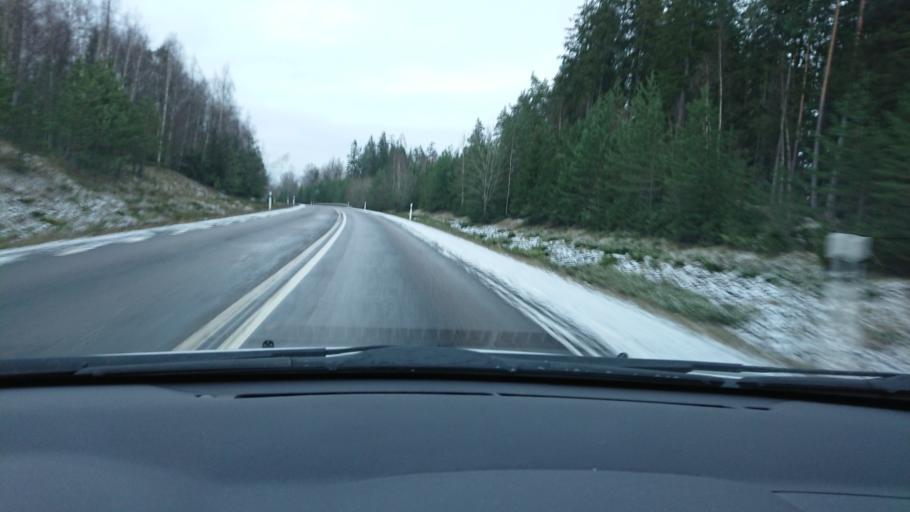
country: SE
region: Kalmar
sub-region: Hultsfreds Kommun
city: Virserum
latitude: 57.3552
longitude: 15.6381
